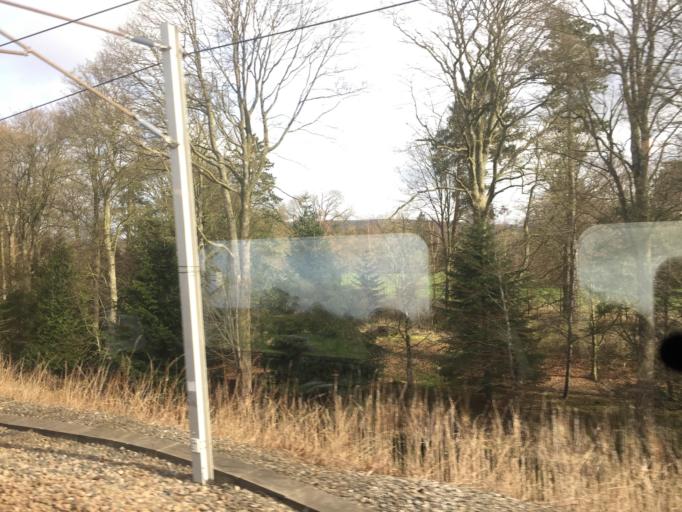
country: GB
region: England
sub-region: Cumbria
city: Penrith
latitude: 54.6490
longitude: -2.7658
